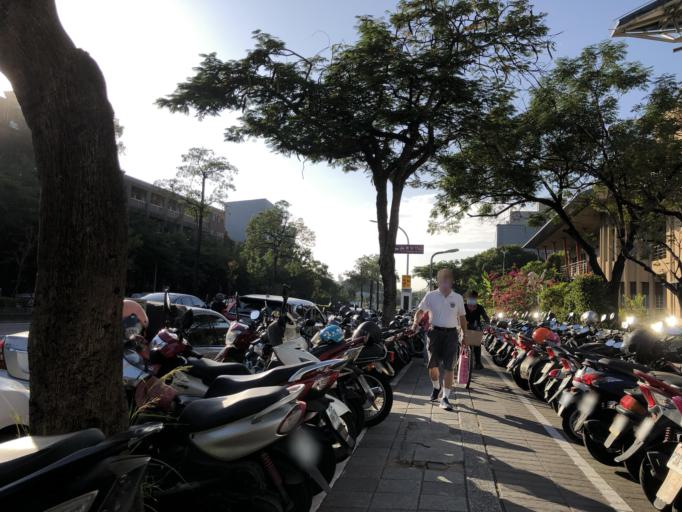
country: TW
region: Taiwan
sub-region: Tainan
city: Tainan
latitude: 23.0014
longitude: 120.2164
